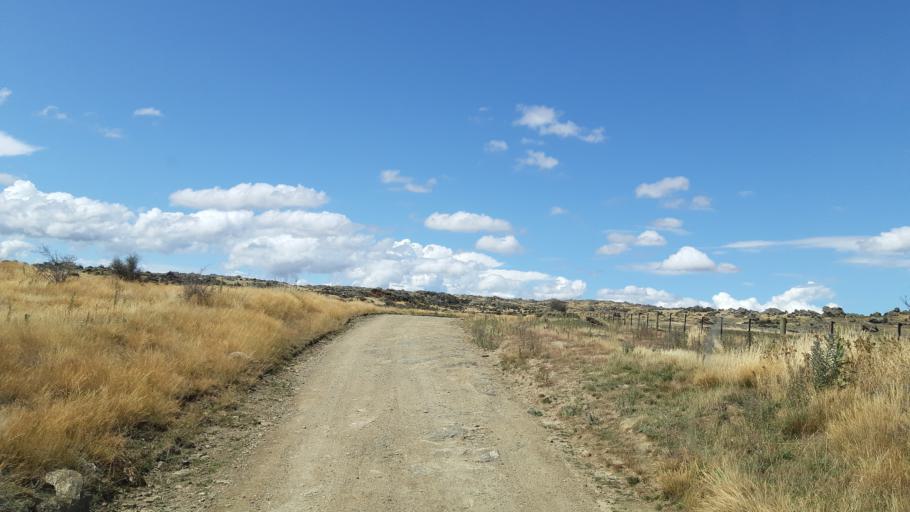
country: NZ
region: Otago
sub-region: Queenstown-Lakes District
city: Wanaka
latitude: -45.2527
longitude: 169.7009
